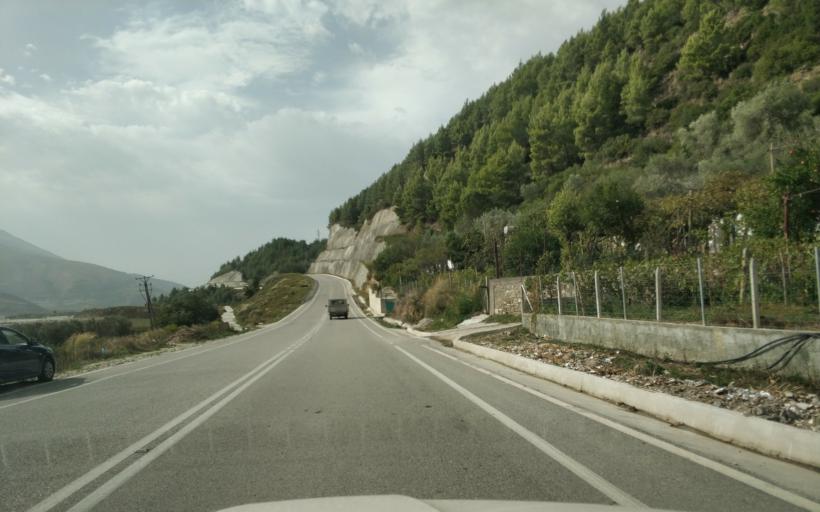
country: AL
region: Gjirokaster
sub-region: Rrethi i Tepelenes
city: Krahes
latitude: 40.3823
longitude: 19.8978
